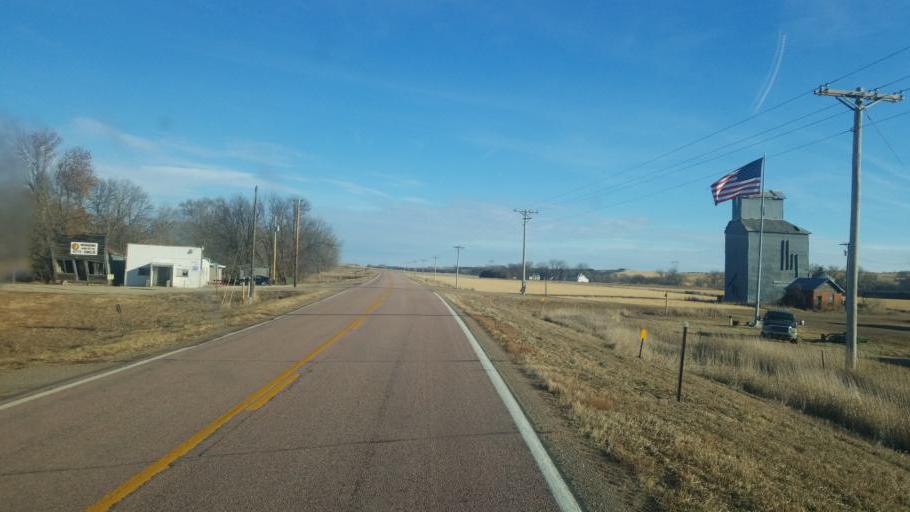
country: US
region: South Dakota
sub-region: Charles Mix County
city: Wagner
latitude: 42.8287
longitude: -98.3307
